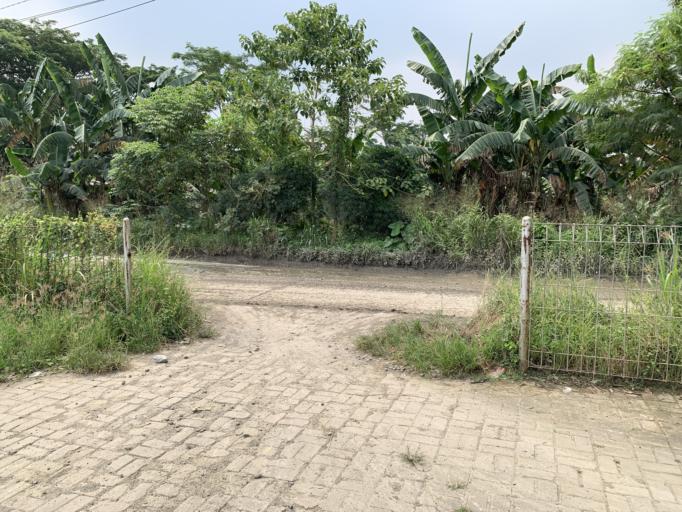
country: ID
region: West Java
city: Serpong
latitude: -6.3832
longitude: 106.6361
